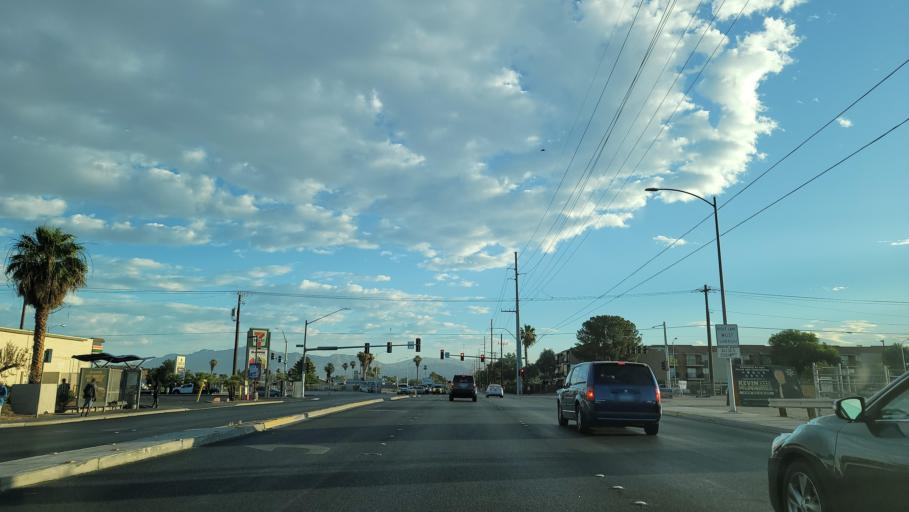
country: US
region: Nevada
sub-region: Clark County
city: North Las Vegas
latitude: 36.1948
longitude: -115.0983
